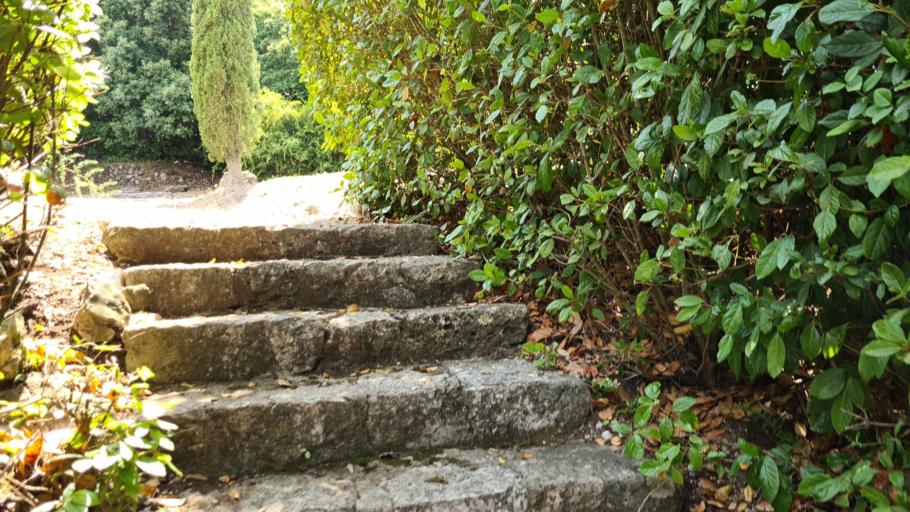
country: FR
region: Provence-Alpes-Cote d'Azur
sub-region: Departement des Alpes-Maritimes
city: La Turbie
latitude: 43.7445
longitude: 7.4029
